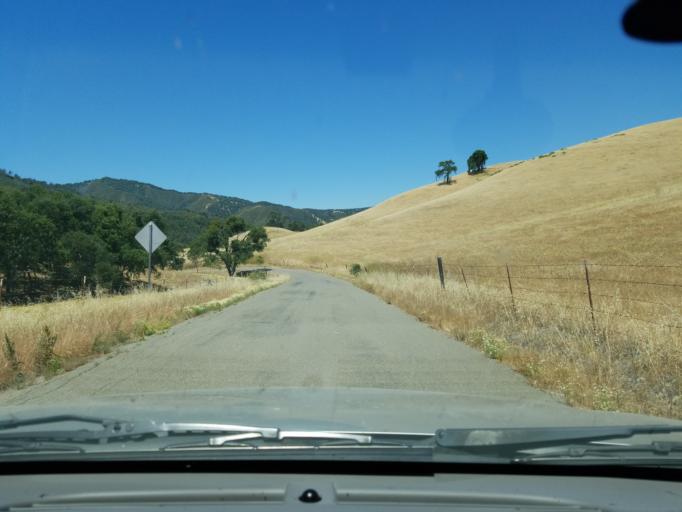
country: US
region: California
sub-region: Monterey County
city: Gonzales
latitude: 36.3368
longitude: -121.5285
